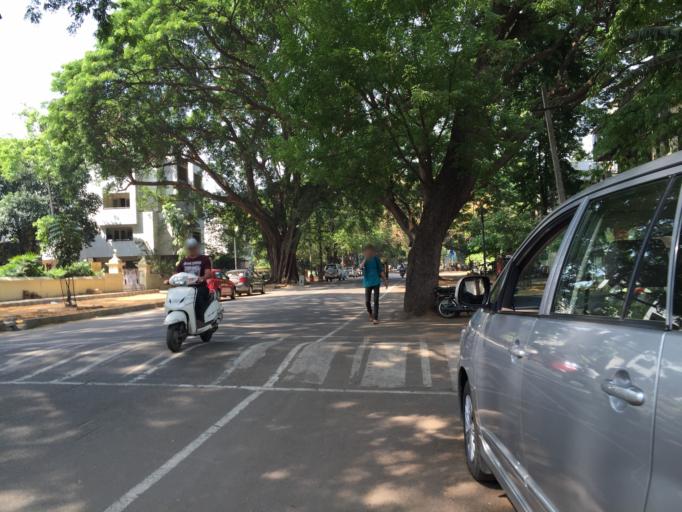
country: IN
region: Karnataka
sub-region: Bangalore Urban
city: Bangalore
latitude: 12.9474
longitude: 77.5794
